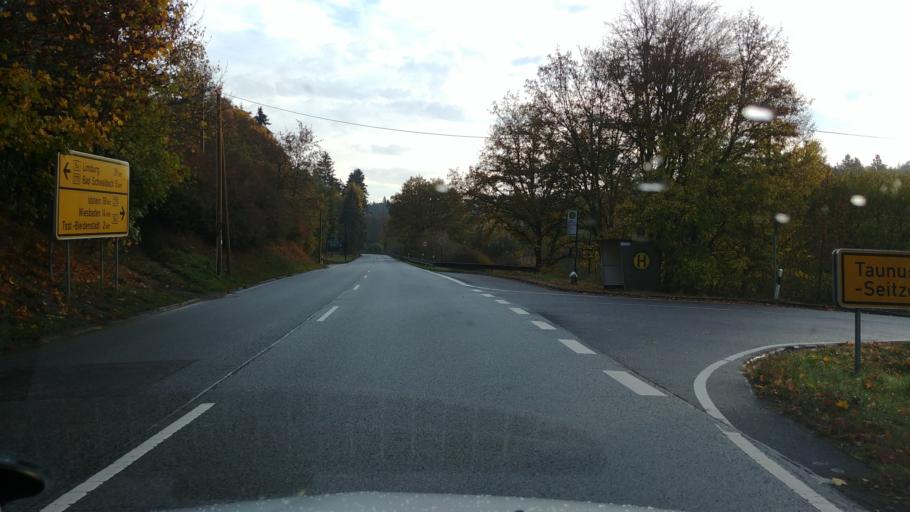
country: DE
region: Hesse
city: Taunusstein
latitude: 50.1324
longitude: 8.1194
